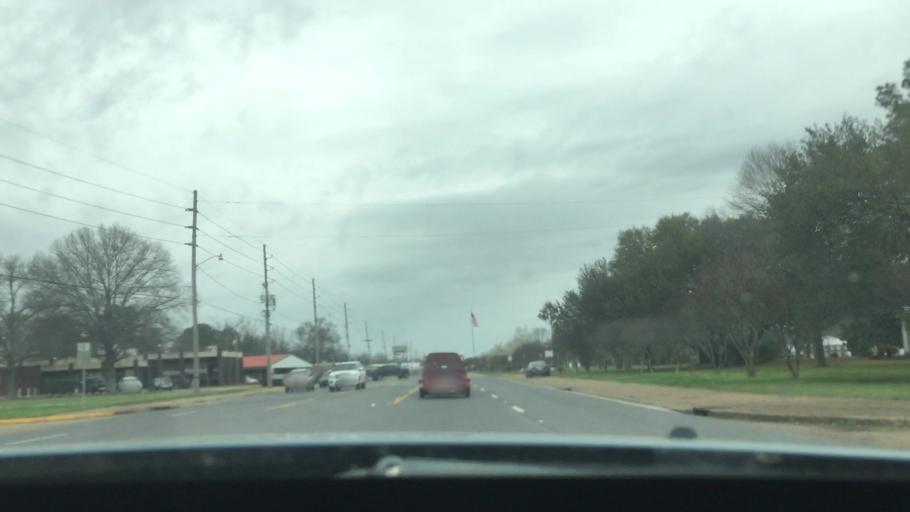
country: US
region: Louisiana
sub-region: Franklin Parish
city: Winnsboro
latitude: 32.1588
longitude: -91.7166
